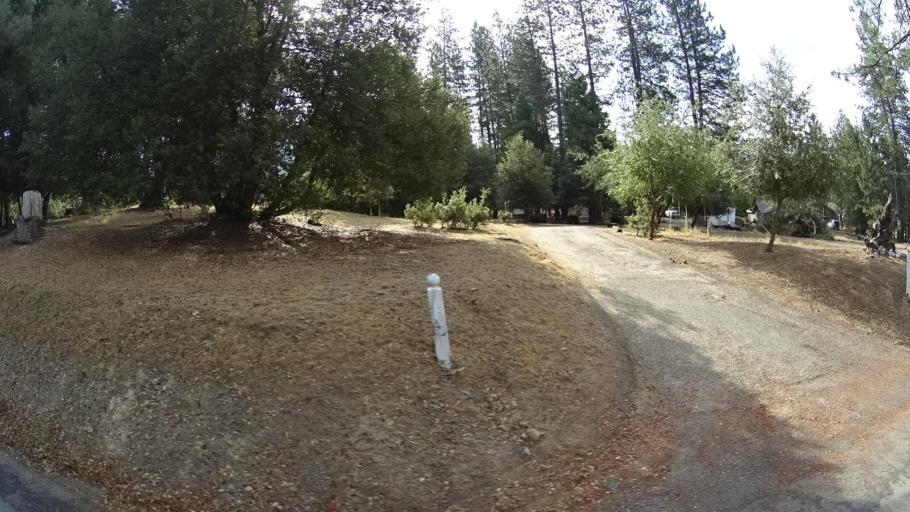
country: US
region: California
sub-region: Madera County
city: Ahwahnee
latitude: 37.4657
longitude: -119.7394
